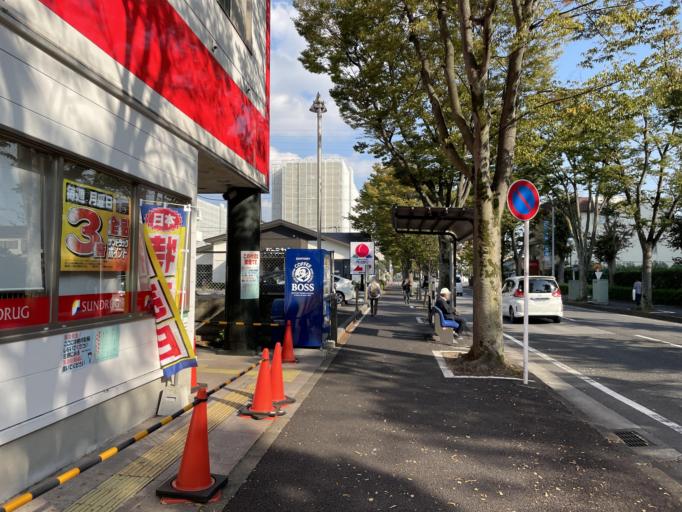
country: JP
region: Chiba
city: Nagareyama
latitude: 35.8278
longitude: 139.9085
